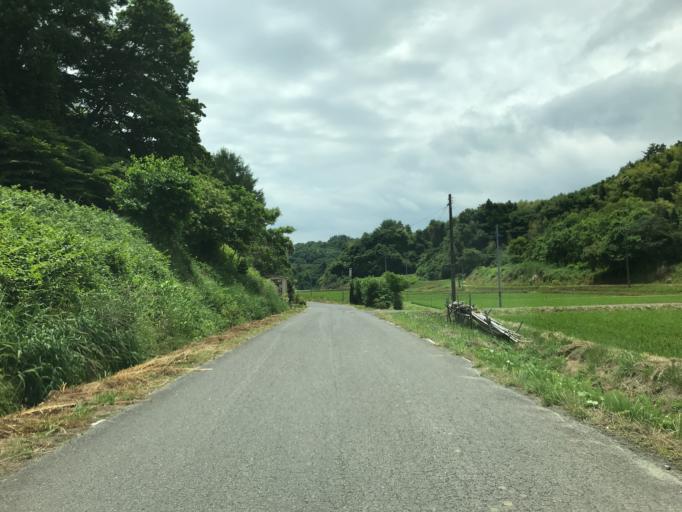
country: JP
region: Fukushima
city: Miharu
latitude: 37.4017
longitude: 140.5233
